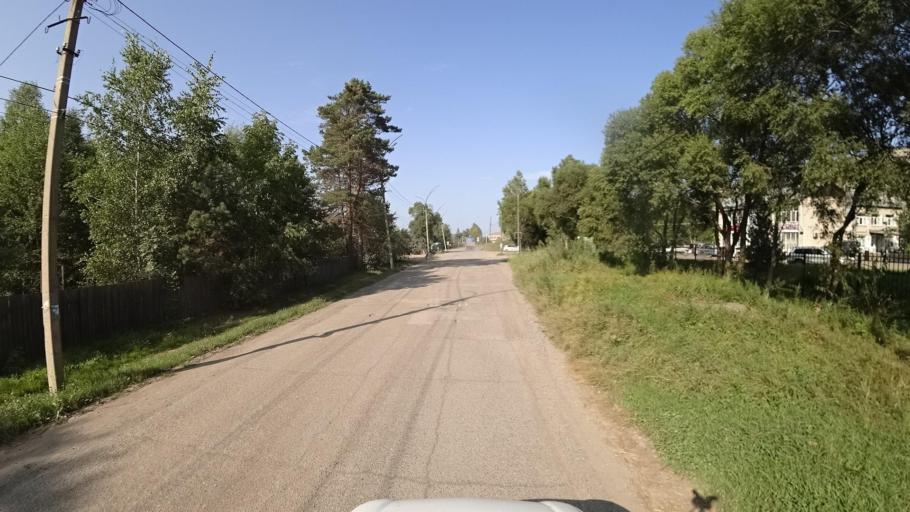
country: RU
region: Khabarovsk Krai
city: Khor
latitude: 47.9727
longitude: 135.0539
